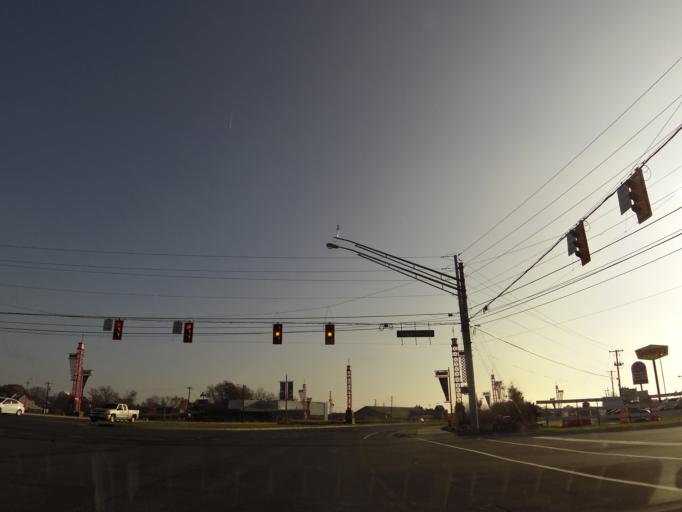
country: US
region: Indiana
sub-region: Marion County
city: Speedway
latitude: 39.8012
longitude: -86.2702
